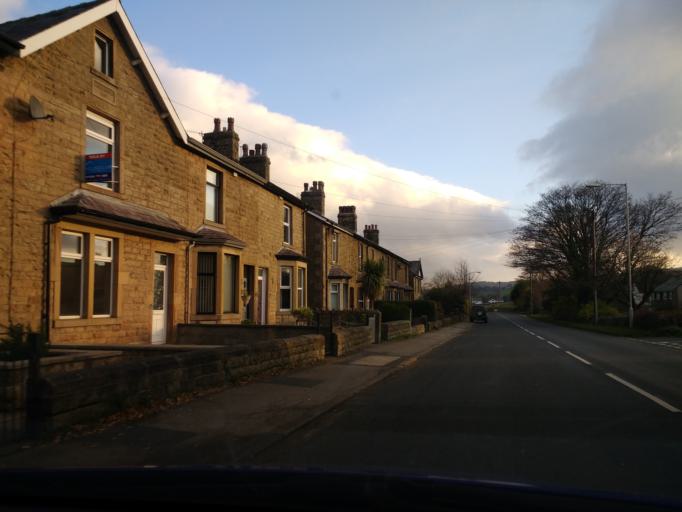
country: GB
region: England
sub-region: Lancashire
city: Caton
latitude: 54.0766
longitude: -2.7150
